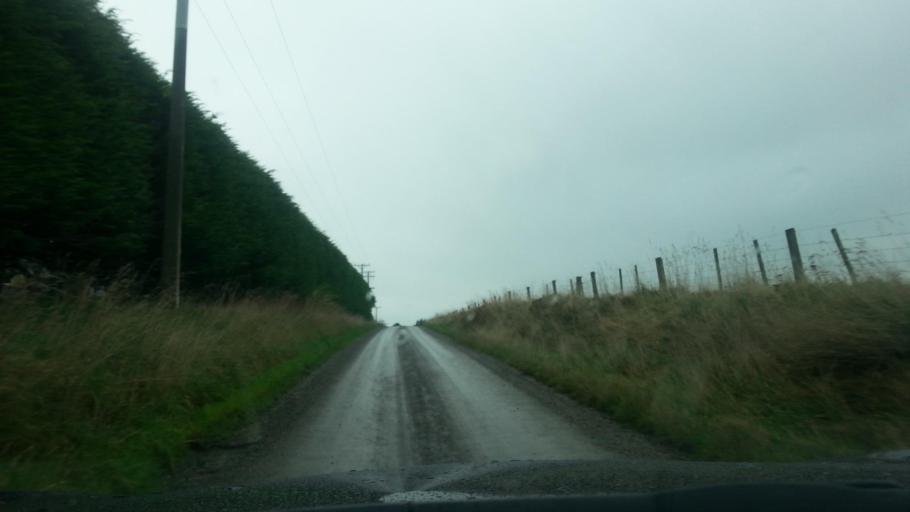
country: NZ
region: Southland
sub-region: Invercargill City
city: Invercargill
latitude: -46.3387
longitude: 168.4064
